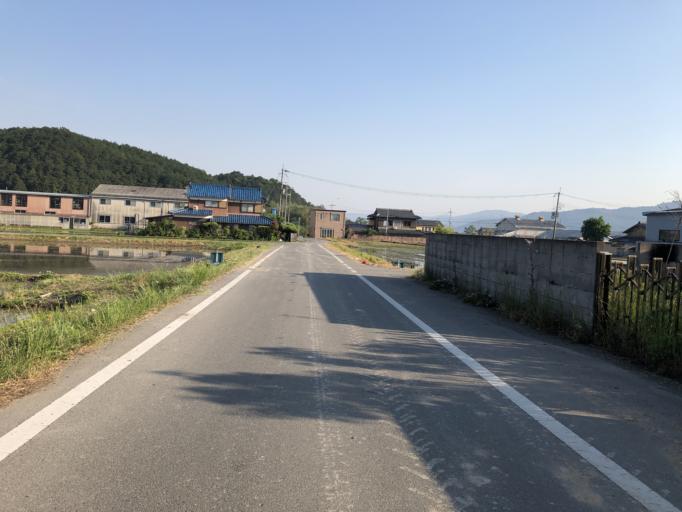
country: JP
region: Kyoto
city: Kameoka
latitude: 35.0730
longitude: 135.5568
